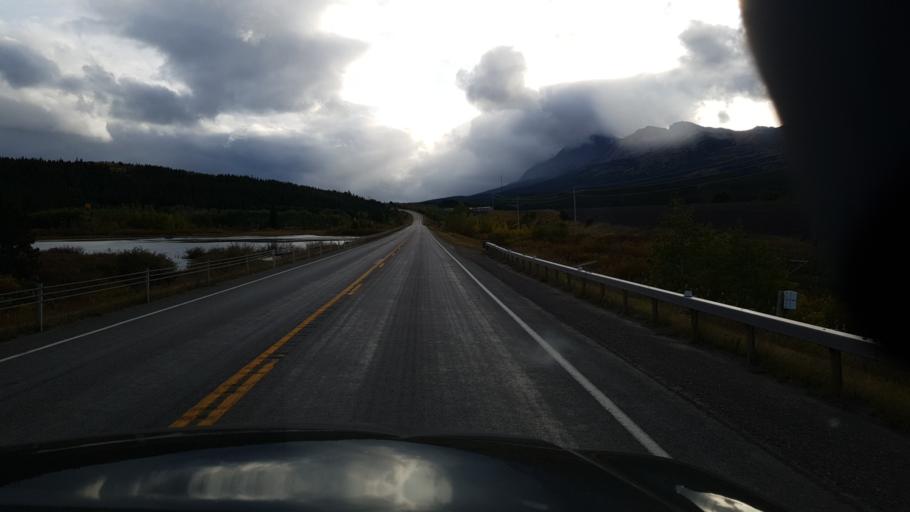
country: US
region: Montana
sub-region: Glacier County
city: South Browning
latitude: 48.3883
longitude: -113.2622
